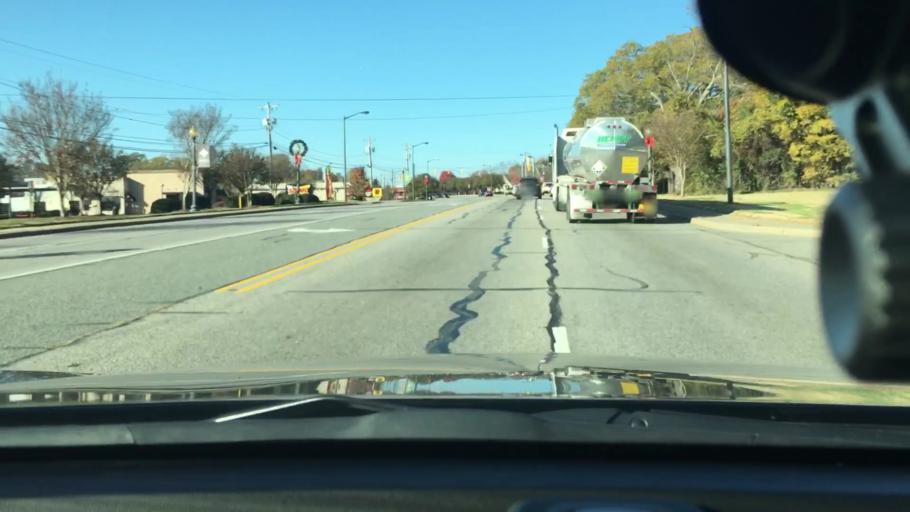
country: US
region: North Carolina
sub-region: Cabarrus County
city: Harrisburg
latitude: 35.3206
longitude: -80.6674
